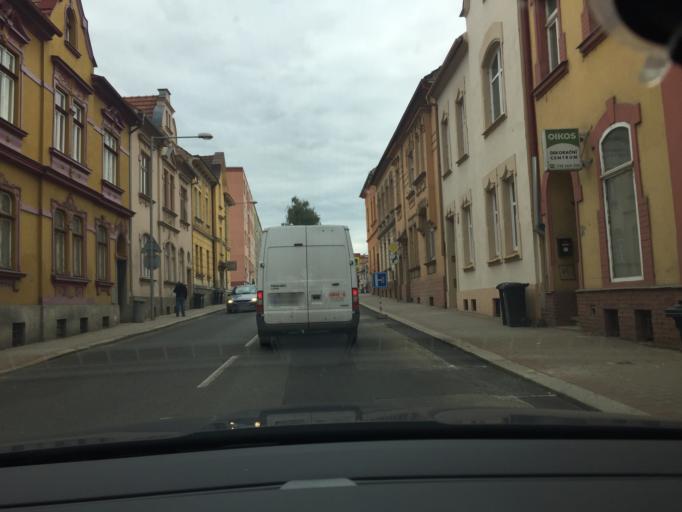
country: CZ
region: Ustecky
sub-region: Okres Litomerice
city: Litomerice
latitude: 50.5361
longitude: 14.1246
